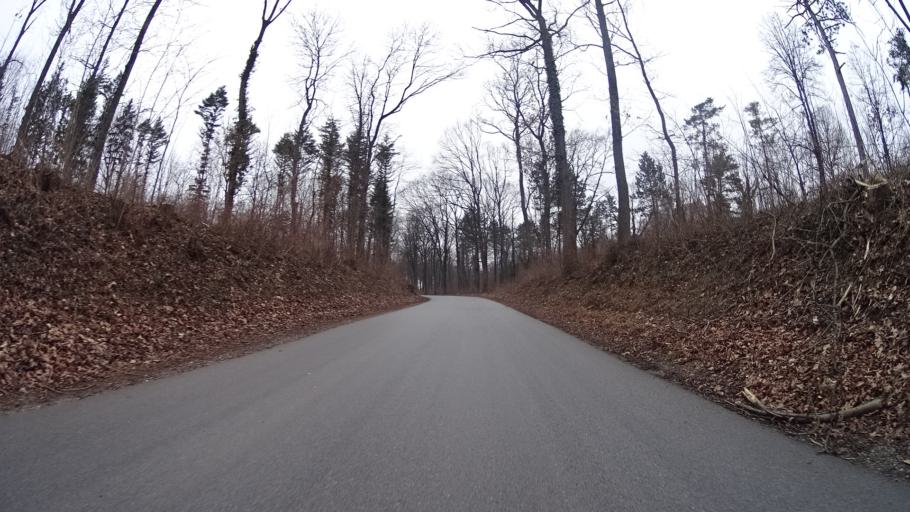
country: AT
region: Lower Austria
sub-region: Politischer Bezirk Korneuburg
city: Leobendorf
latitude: 48.3755
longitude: 16.3083
